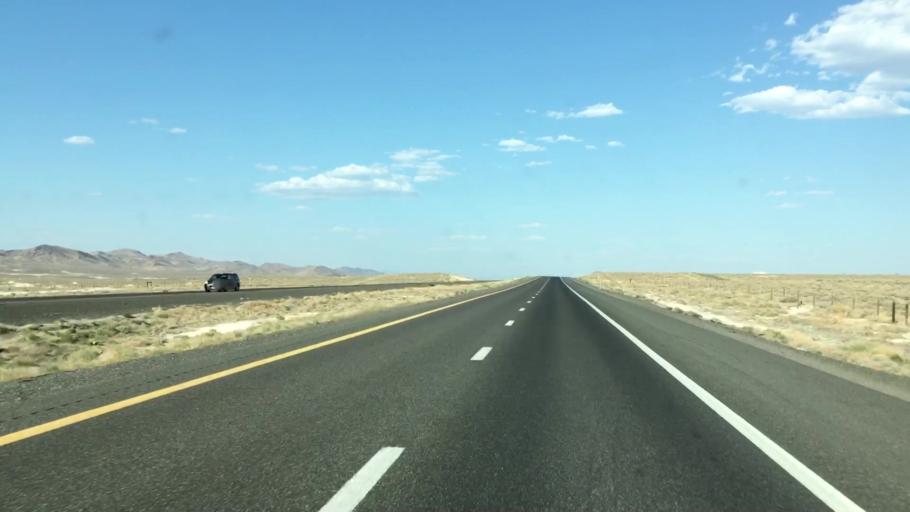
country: US
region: Nevada
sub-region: Lyon County
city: Fernley
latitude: 39.8340
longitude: -118.9600
